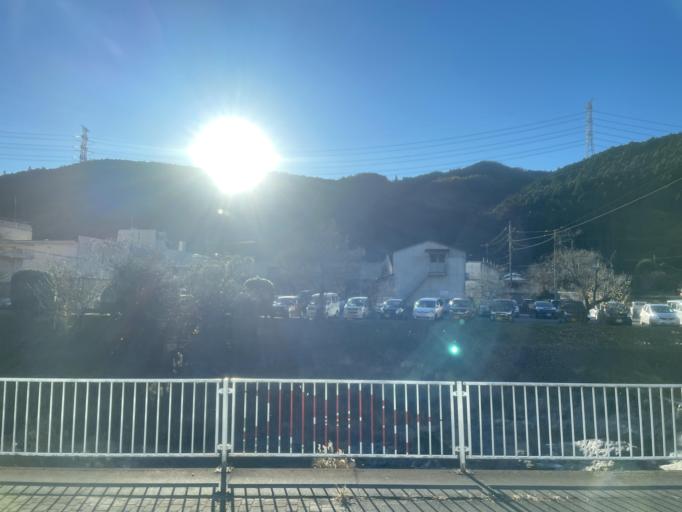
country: JP
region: Saitama
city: Yorii
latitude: 36.0590
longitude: 139.1949
